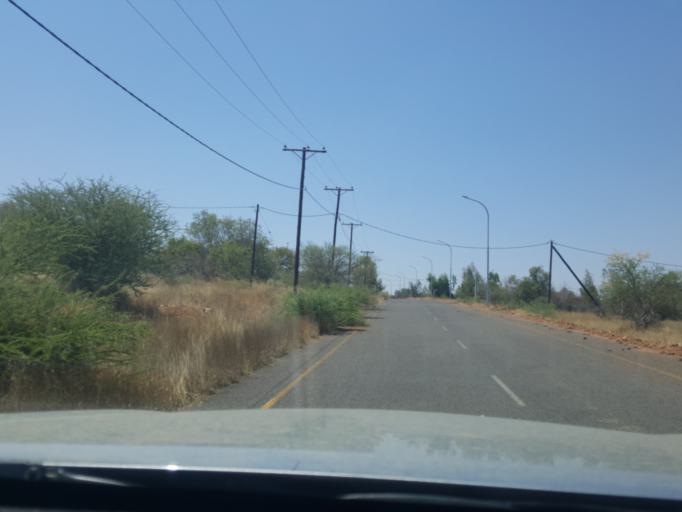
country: BW
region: South East
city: Lobatse
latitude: -25.1823
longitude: 25.6810
